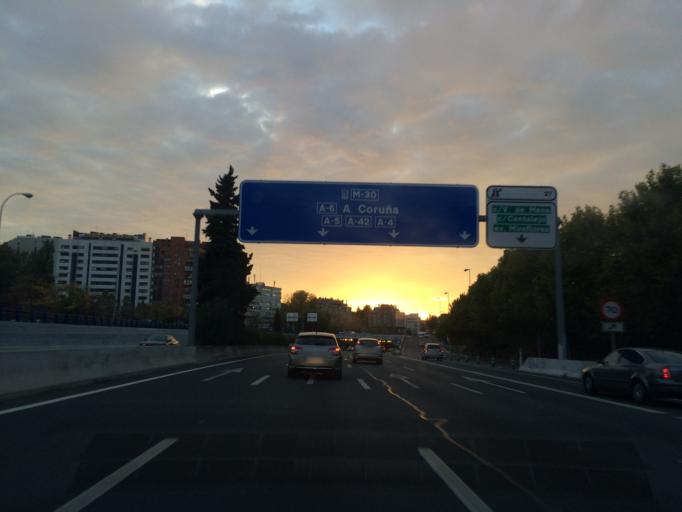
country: ES
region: Madrid
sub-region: Provincia de Madrid
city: Tetuan de las Victorias
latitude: 40.4739
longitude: -3.7251
